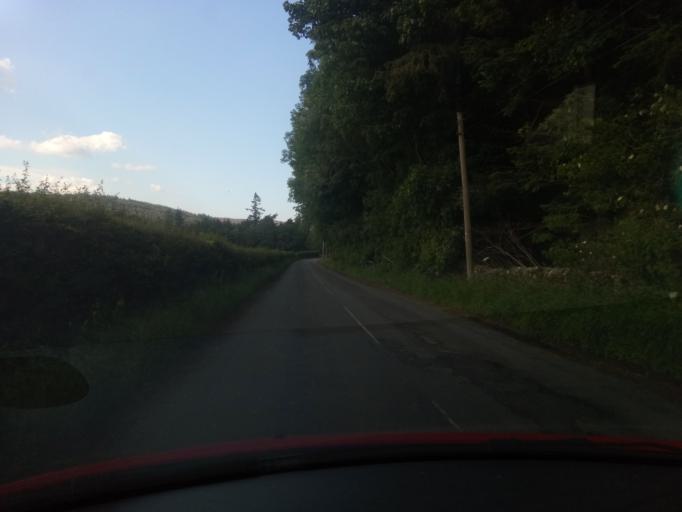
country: GB
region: Scotland
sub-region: The Scottish Borders
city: Selkirk
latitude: 55.5220
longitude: -2.9241
